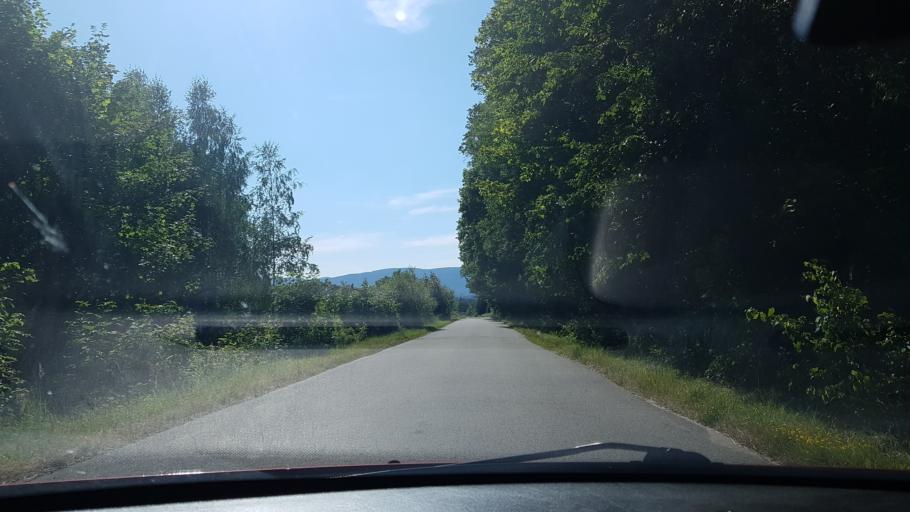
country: PL
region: Lower Silesian Voivodeship
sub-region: Powiat klodzki
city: Miedzylesie
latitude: 50.2334
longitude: 16.7312
